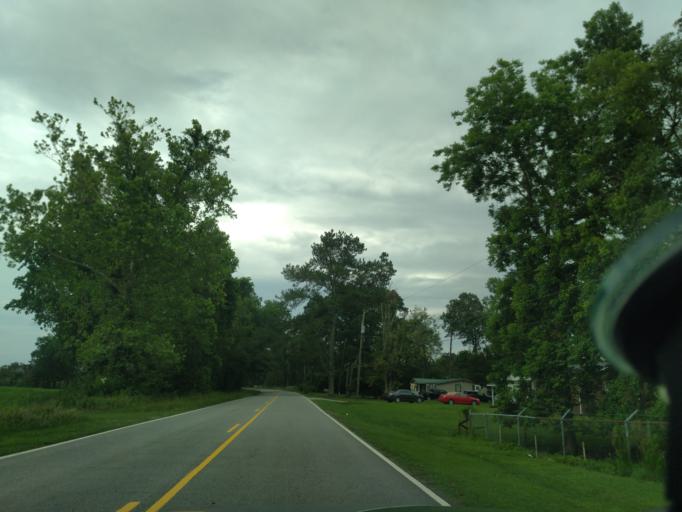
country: US
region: North Carolina
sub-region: Washington County
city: Plymouth
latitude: 35.8789
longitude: -76.6066
